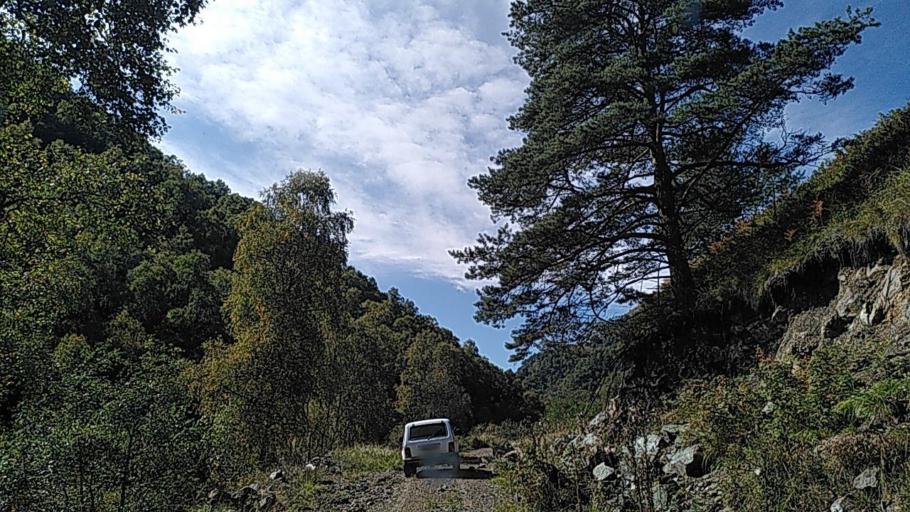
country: RU
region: Kabardino-Balkariya
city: Kamennomostskoye
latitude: 43.6928
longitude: 42.8350
